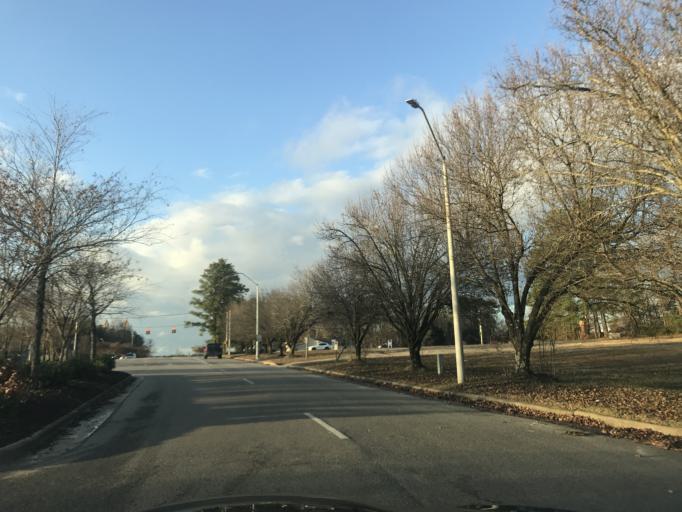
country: US
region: North Carolina
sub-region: Wake County
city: Rolesville
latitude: 35.9179
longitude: -78.4640
